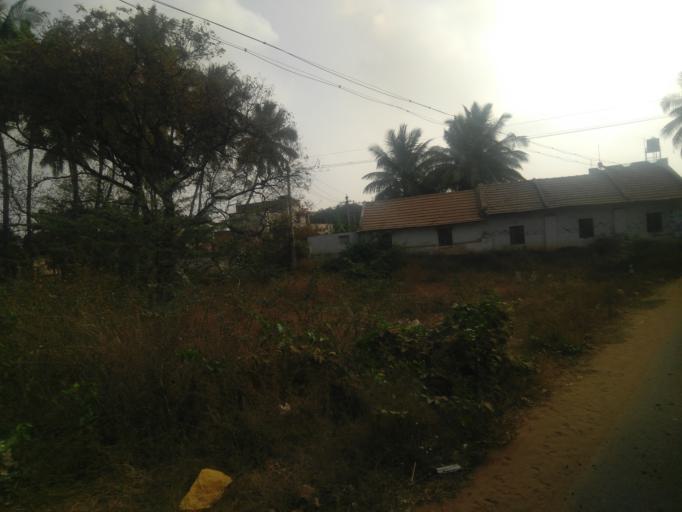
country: IN
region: Tamil Nadu
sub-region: Coimbatore
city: Perur
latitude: 11.0538
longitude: 76.8972
